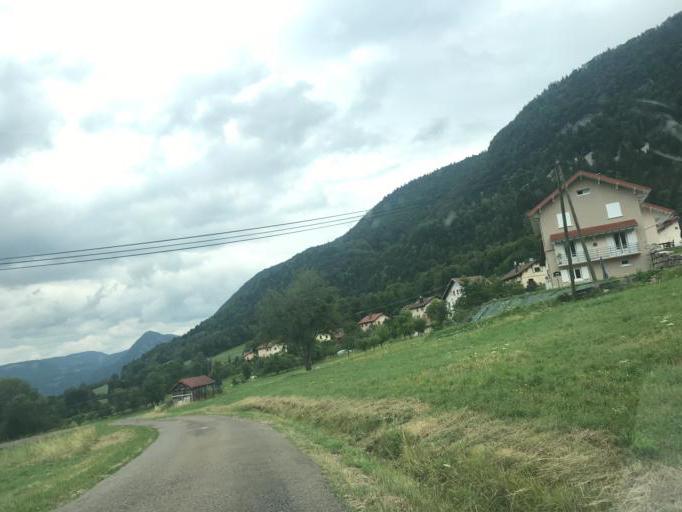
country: FR
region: Franche-Comte
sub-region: Departement du Jura
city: Saint-Claude
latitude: 46.3419
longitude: 5.8401
